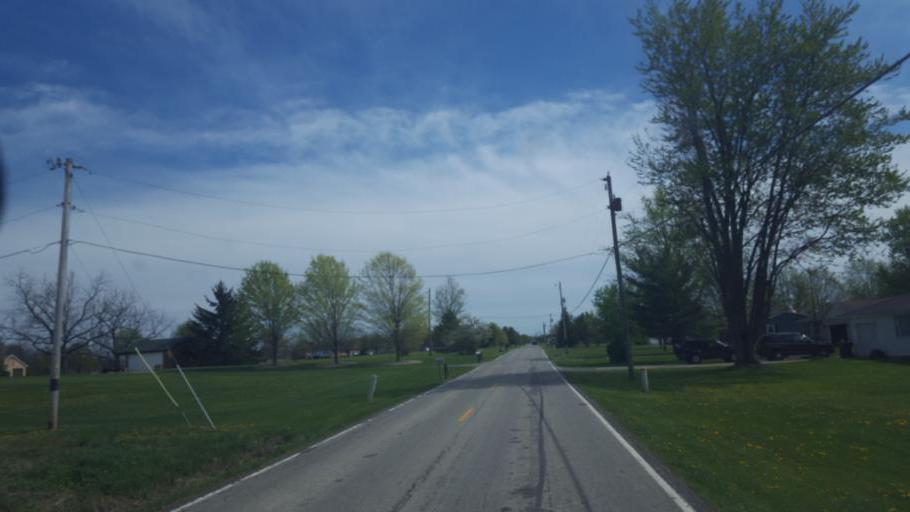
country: US
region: Ohio
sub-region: Richland County
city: Shelby
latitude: 40.8655
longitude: -82.6130
